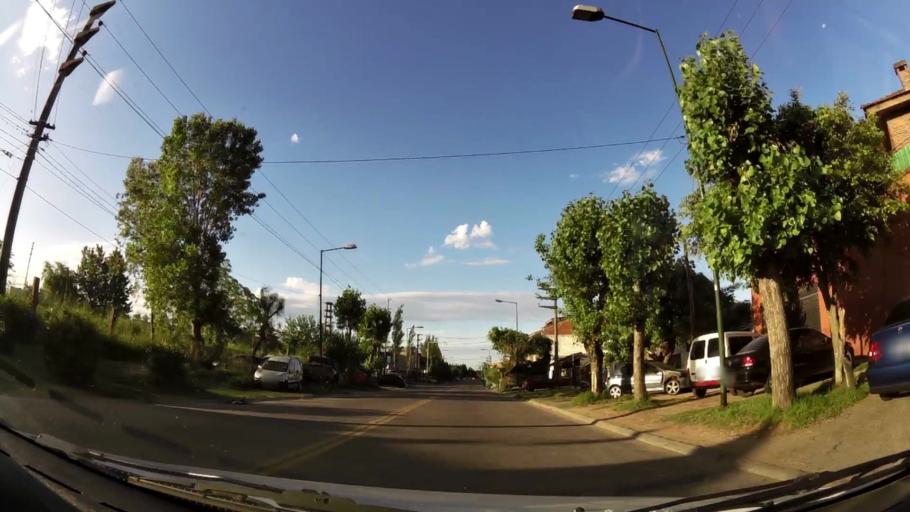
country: AR
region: Buenos Aires
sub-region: Partido de San Isidro
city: San Isidro
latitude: -34.4692
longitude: -58.5552
